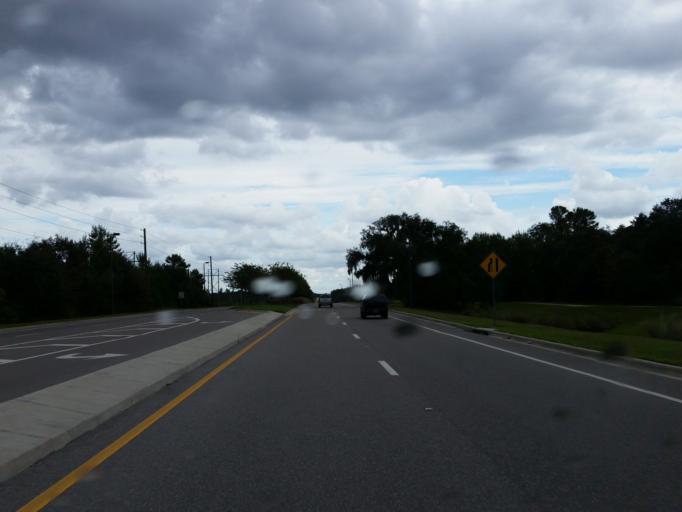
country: US
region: Florida
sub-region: Hillsborough County
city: Bloomingdale
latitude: 27.8542
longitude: -82.2551
